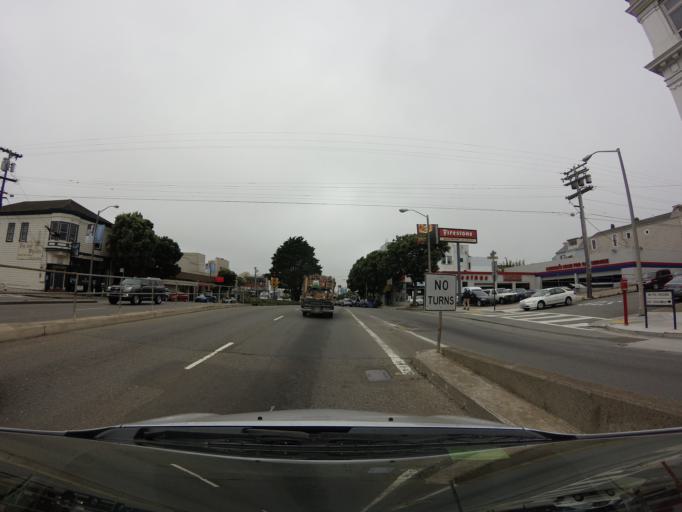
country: US
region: California
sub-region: San Francisco County
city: San Francisco
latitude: 37.7823
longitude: -122.4490
